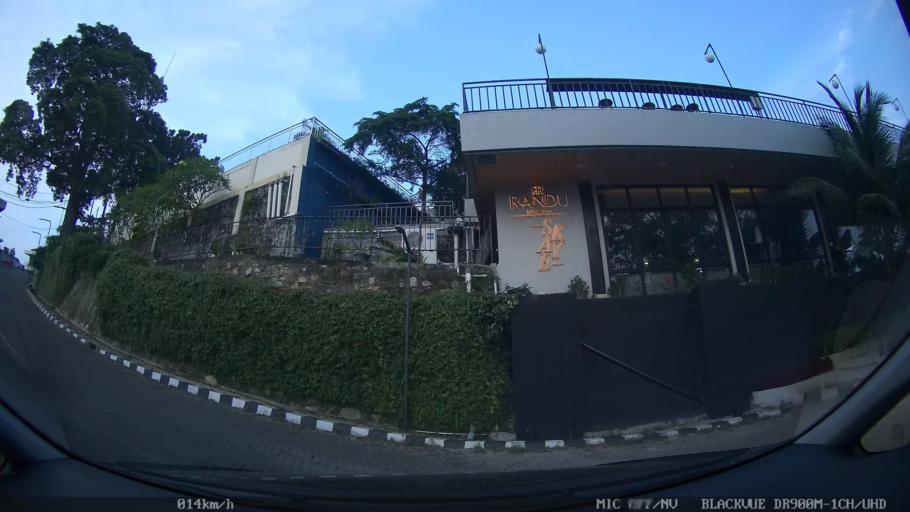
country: ID
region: Lampung
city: Bandarlampung
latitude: -5.4106
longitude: 105.2627
